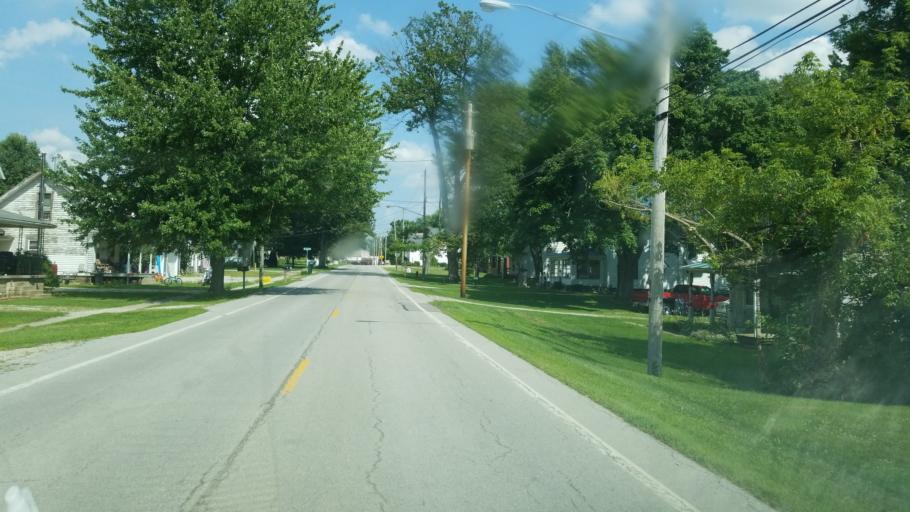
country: US
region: Ohio
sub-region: Huron County
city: Plymouth
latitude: 41.1041
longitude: -82.6164
